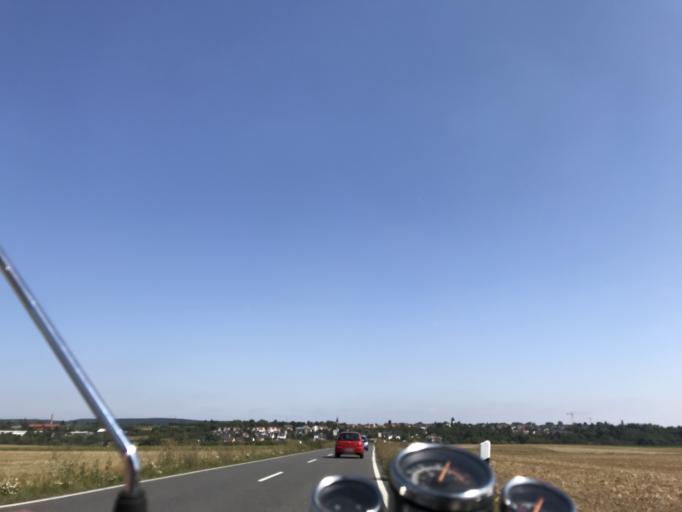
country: DE
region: Hesse
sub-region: Regierungsbezirk Darmstadt
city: Wiesbaden
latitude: 50.0821
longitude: 8.3090
